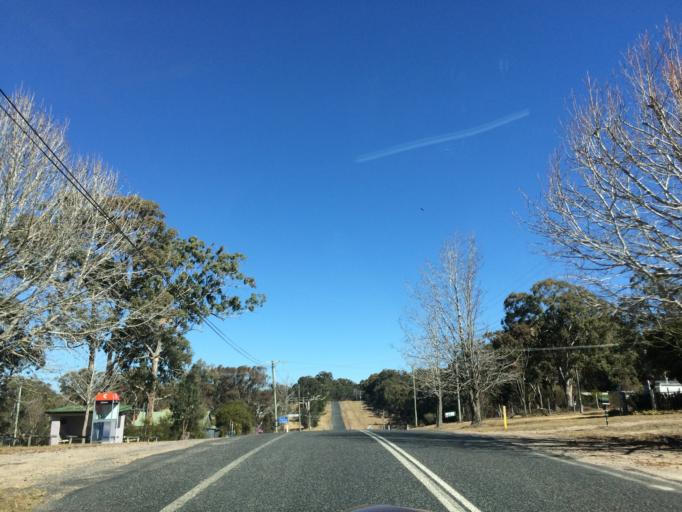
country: AU
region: Queensland
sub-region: Southern Downs
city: Stanthorpe
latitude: -28.6459
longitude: 152.0850
